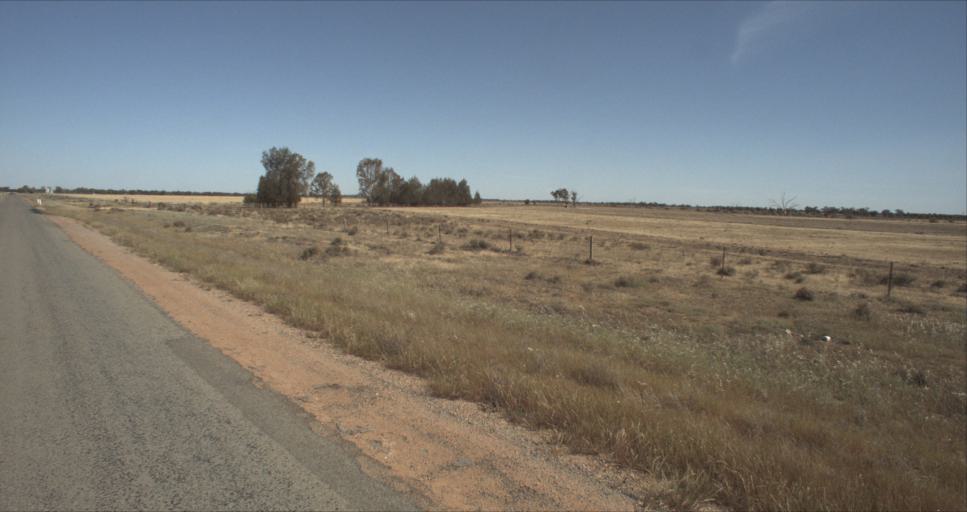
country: AU
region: New South Wales
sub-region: Leeton
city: Leeton
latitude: -34.4892
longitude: 146.3811
